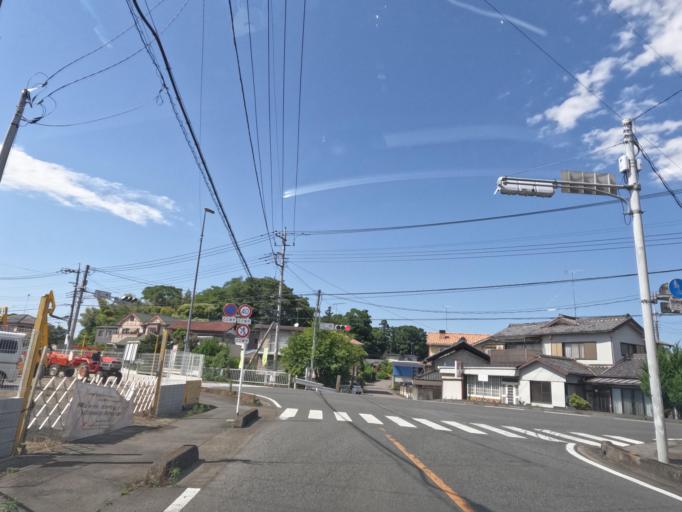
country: JP
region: Saitama
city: Kumagaya
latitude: 36.0955
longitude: 139.3974
